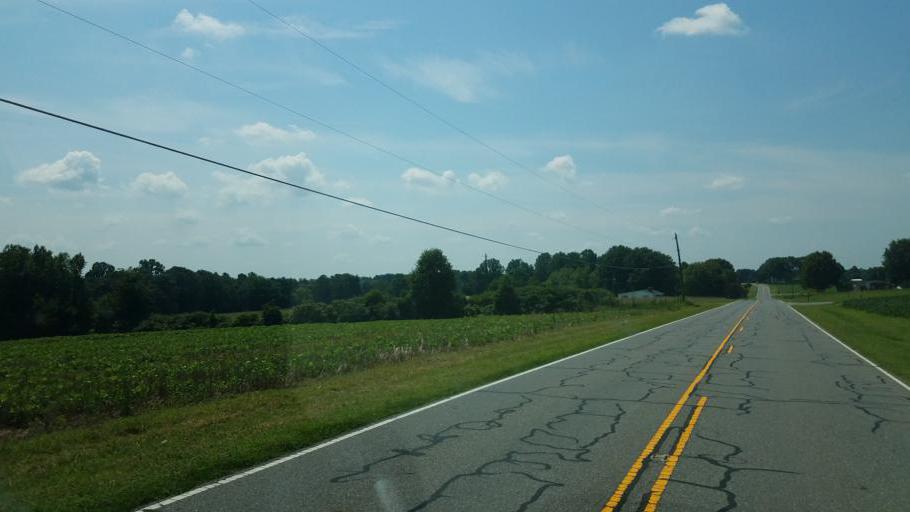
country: US
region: North Carolina
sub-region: Gaston County
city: Cherryville
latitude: 35.4809
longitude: -81.4440
